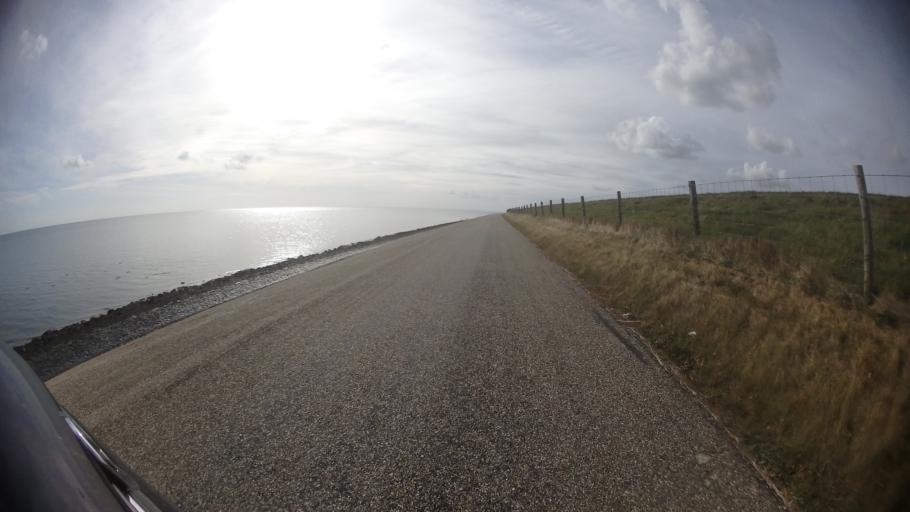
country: NL
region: North Holland
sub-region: Gemeente Texel
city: Den Burg
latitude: 53.0884
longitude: 4.9002
